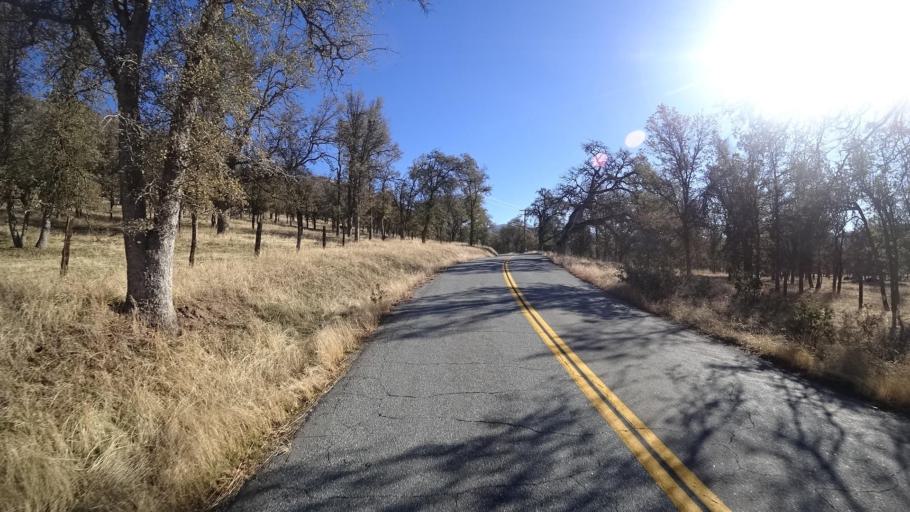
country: US
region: California
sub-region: Kern County
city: Alta Sierra
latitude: 35.7982
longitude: -118.7175
